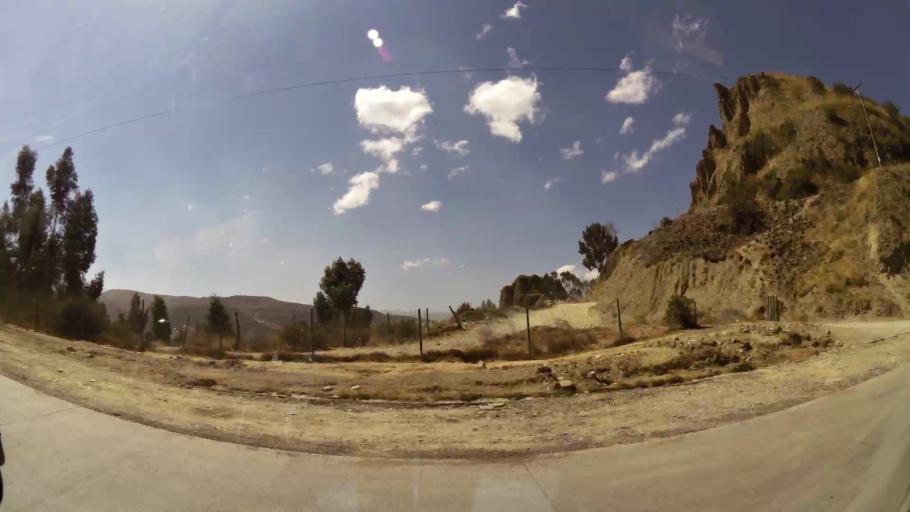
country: BO
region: La Paz
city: La Paz
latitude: -16.4837
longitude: -68.1594
